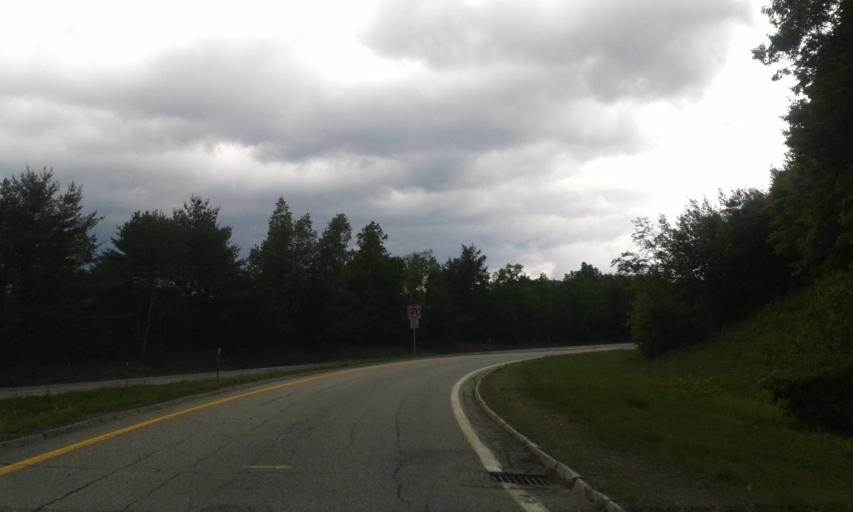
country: US
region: New Hampshire
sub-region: Grafton County
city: Woodstock
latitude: 43.9573
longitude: -71.6820
